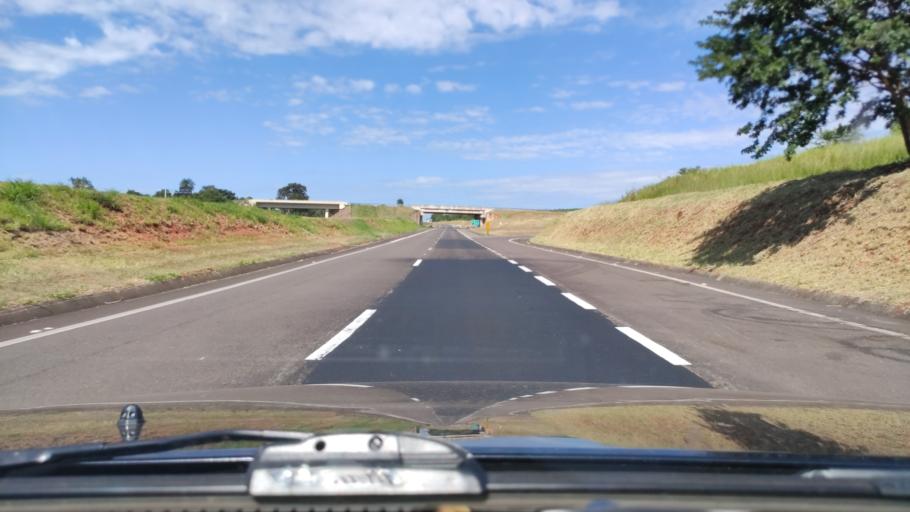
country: BR
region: Sao Paulo
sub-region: Rancharia
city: Rancharia
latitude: -22.4407
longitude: -51.0001
